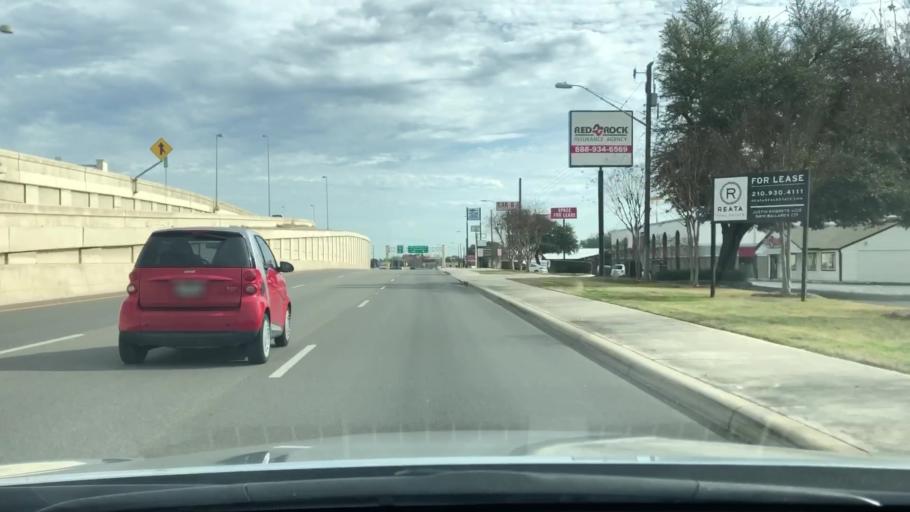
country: US
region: Texas
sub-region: Bexar County
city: Alamo Heights
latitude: 29.5154
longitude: -98.4413
